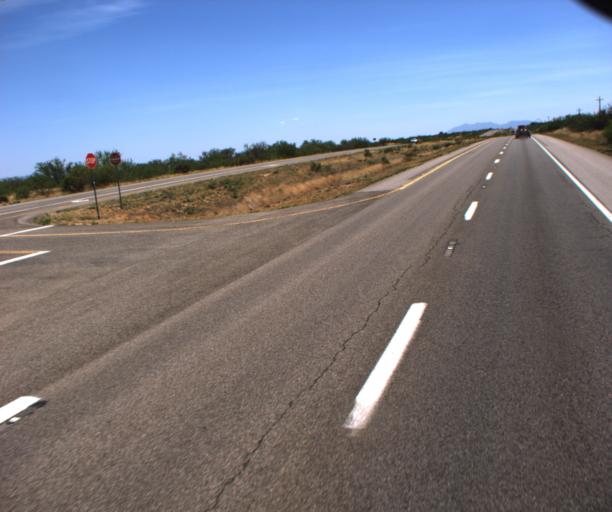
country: US
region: Arizona
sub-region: Cochise County
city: Whetstone
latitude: 31.8919
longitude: -110.3414
